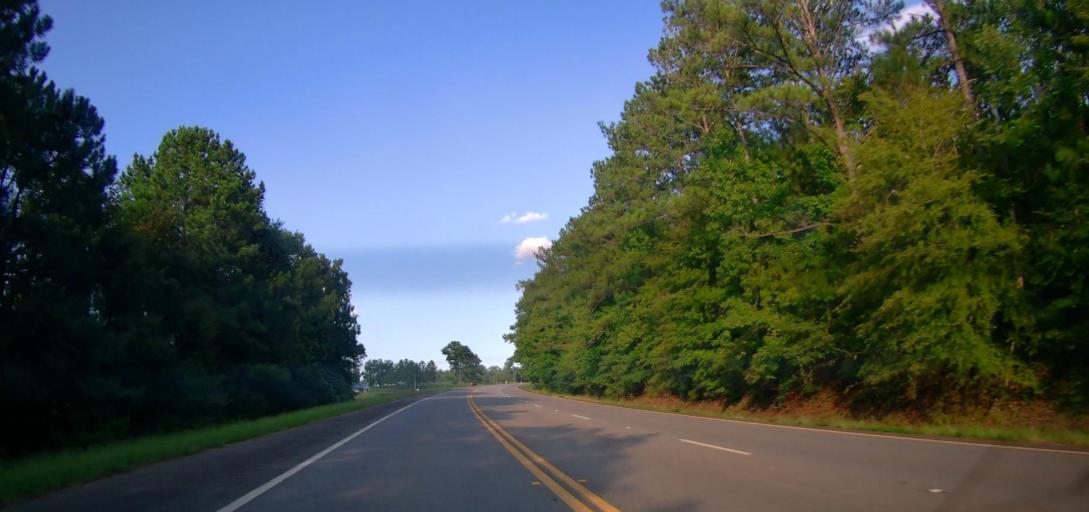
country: US
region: Georgia
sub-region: Bibb County
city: West Point
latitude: 32.8014
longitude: -83.8620
